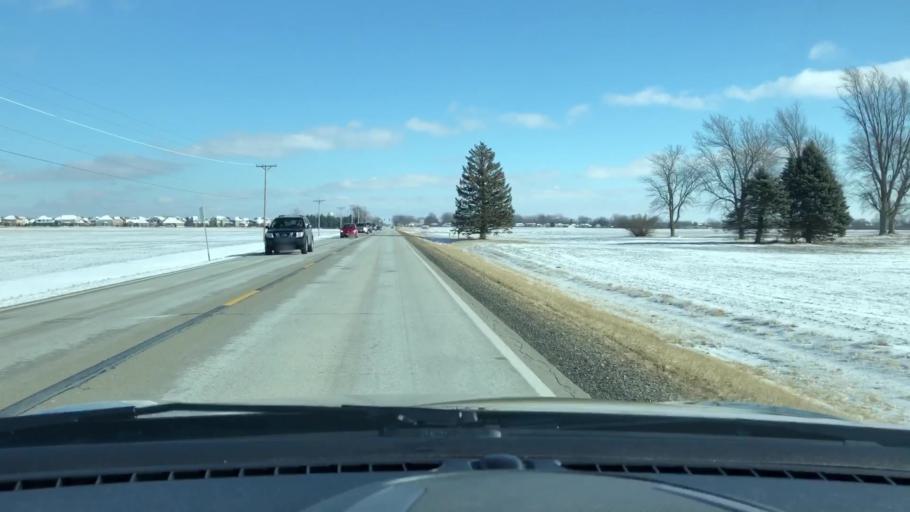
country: US
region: Illinois
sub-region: Will County
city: Ingalls Park
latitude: 41.4825
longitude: -88.0118
